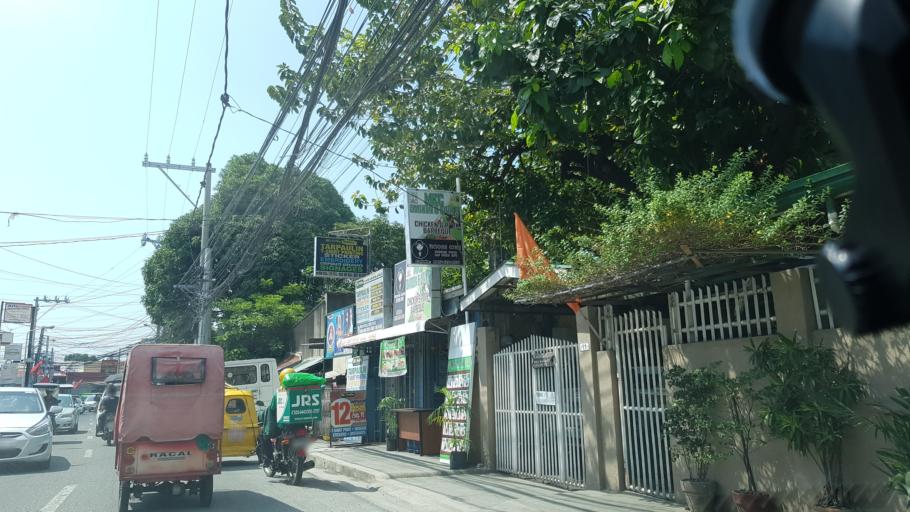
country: PH
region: Calabarzon
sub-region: Province of Rizal
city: Las Pinas
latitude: 14.4676
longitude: 120.9818
